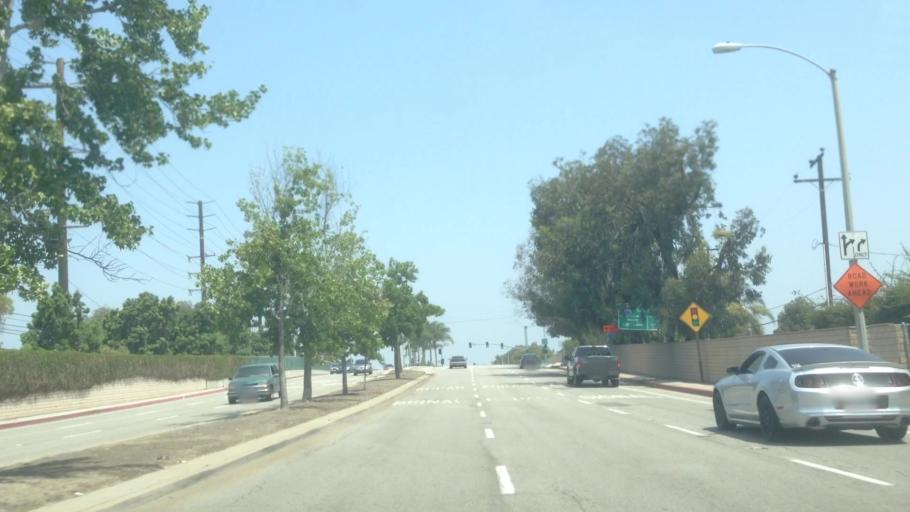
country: US
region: California
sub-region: Orange County
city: Costa Mesa
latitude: 33.6852
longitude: -117.9078
